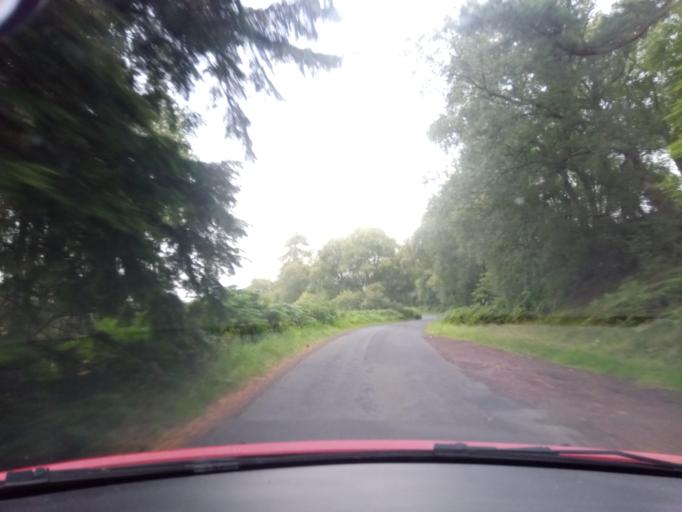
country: GB
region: England
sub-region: Northumberland
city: Otterburn
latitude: 55.2935
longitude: -2.0484
